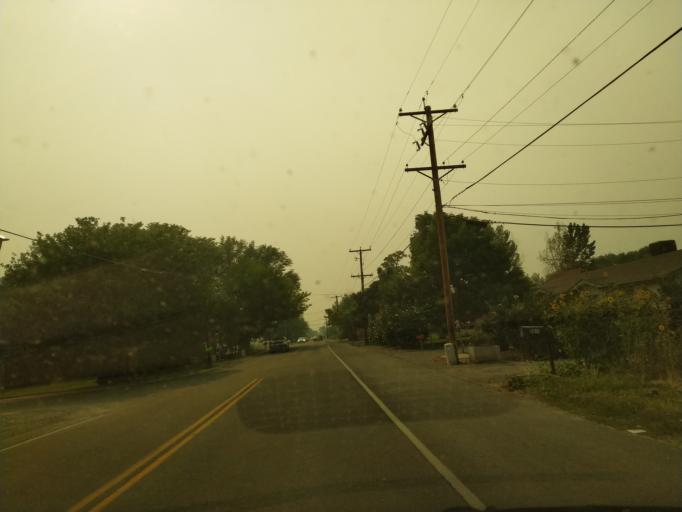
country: US
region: Colorado
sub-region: Mesa County
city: Fruitvale
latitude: 39.0846
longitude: -108.4881
